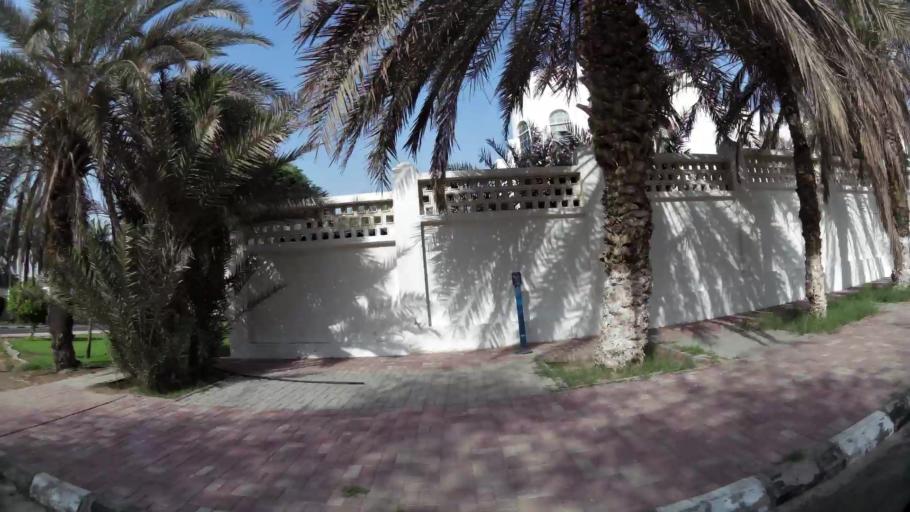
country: AE
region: Ash Shariqah
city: Sharjah
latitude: 25.2485
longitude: 55.4201
